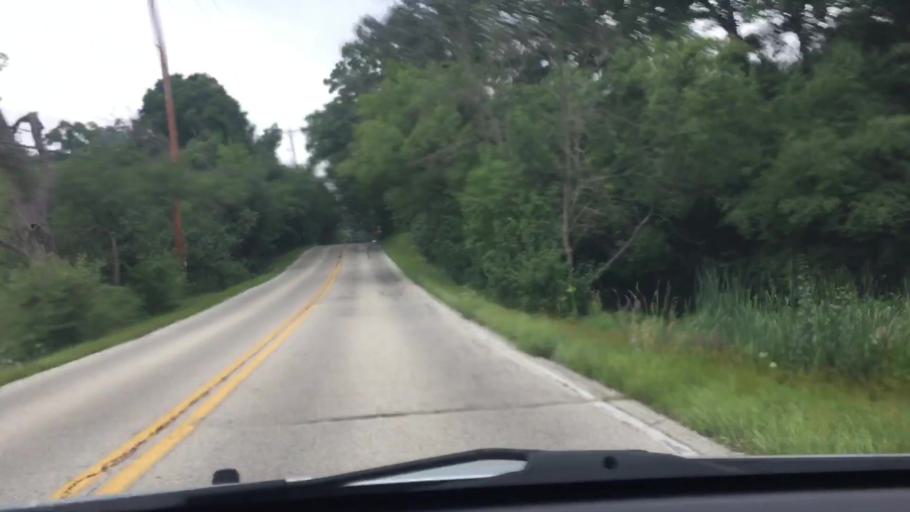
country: US
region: Wisconsin
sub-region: Waukesha County
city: Dousman
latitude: 43.0251
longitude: -88.4428
